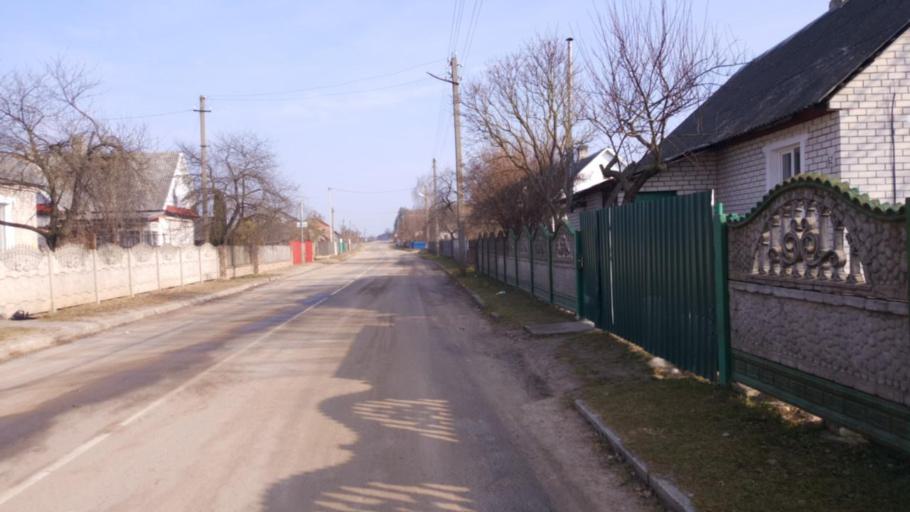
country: BY
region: Brest
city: Kamyanyets
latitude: 52.4069
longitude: 23.8315
